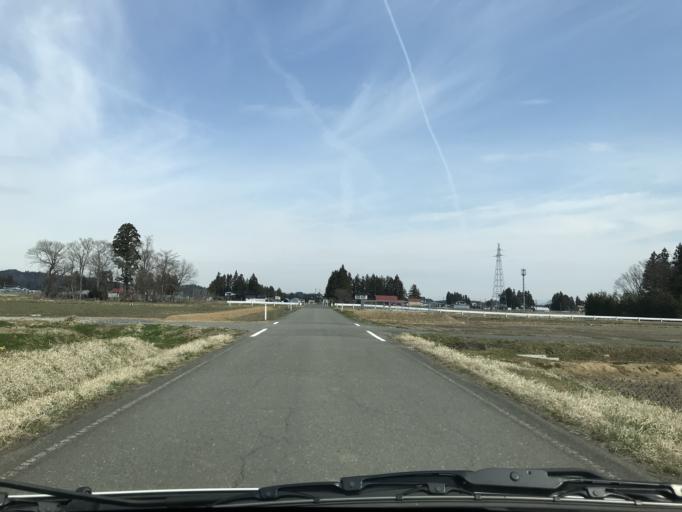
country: JP
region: Iwate
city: Mizusawa
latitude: 39.1246
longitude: 141.0480
